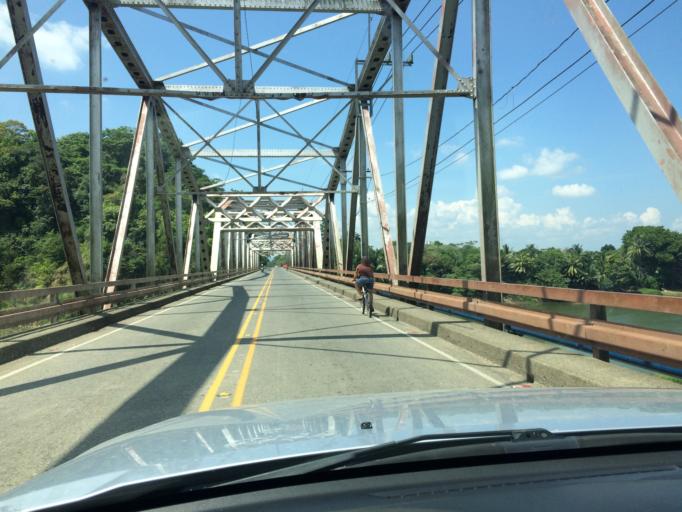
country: CR
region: Puntarenas
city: Ciudad Cortes
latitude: 8.9588
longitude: -83.4600
